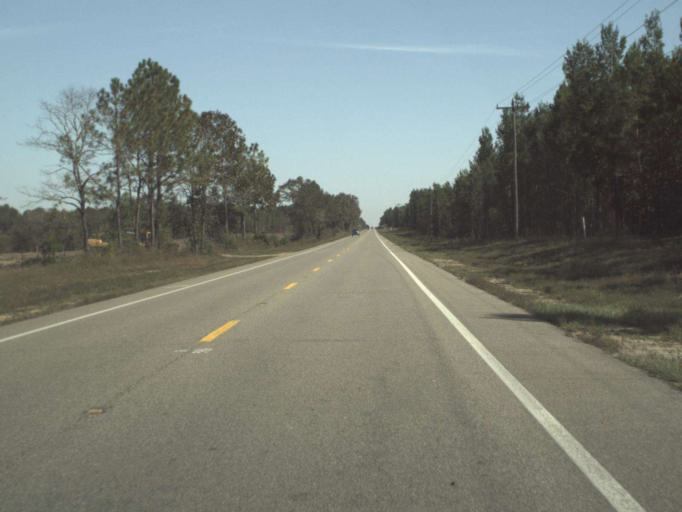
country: US
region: Florida
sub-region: Liberty County
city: Bristol
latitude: 30.4893
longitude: -84.9047
